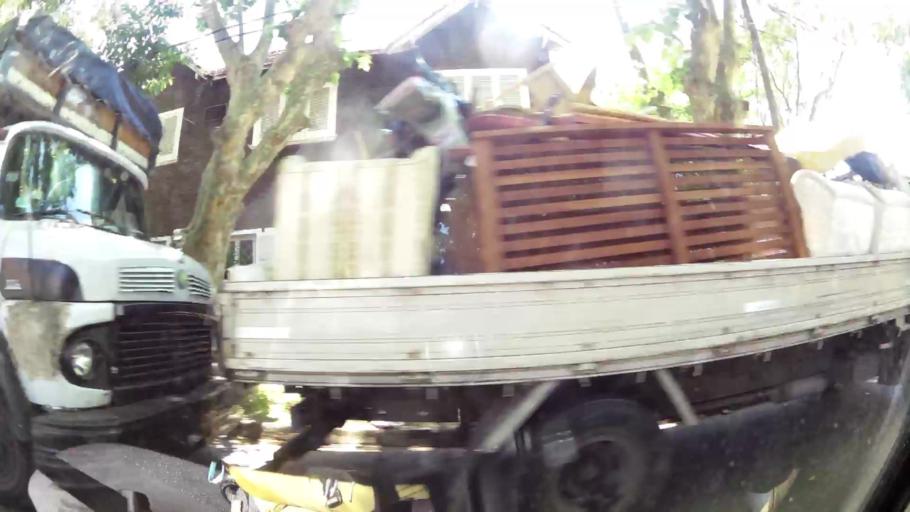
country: AR
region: Buenos Aires
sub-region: Partido de Vicente Lopez
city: Olivos
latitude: -34.4890
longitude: -58.4903
